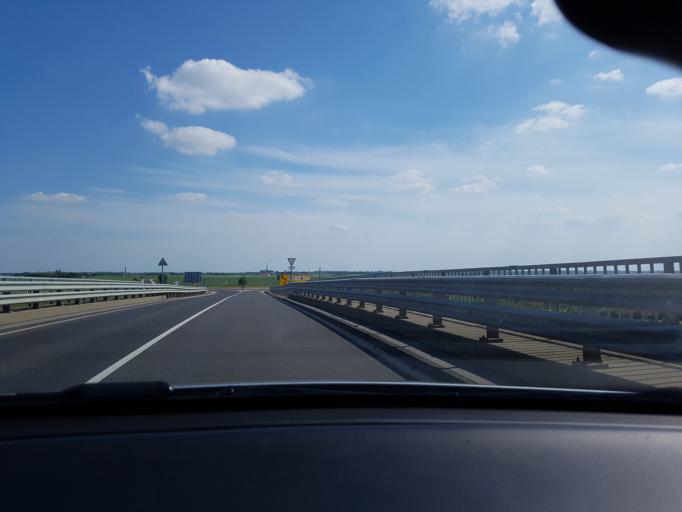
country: HU
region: Csongrad
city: Csanadpalota
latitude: 46.2159
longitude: 20.7149
